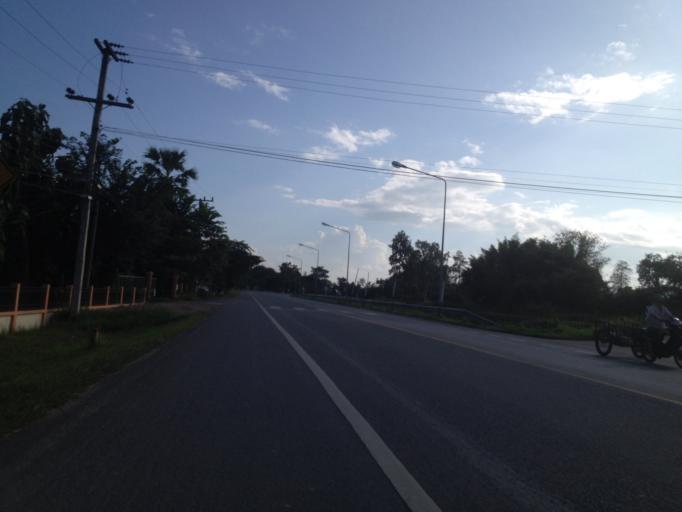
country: TH
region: Chiang Mai
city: San Pa Tong
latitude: 18.6597
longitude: 98.8679
